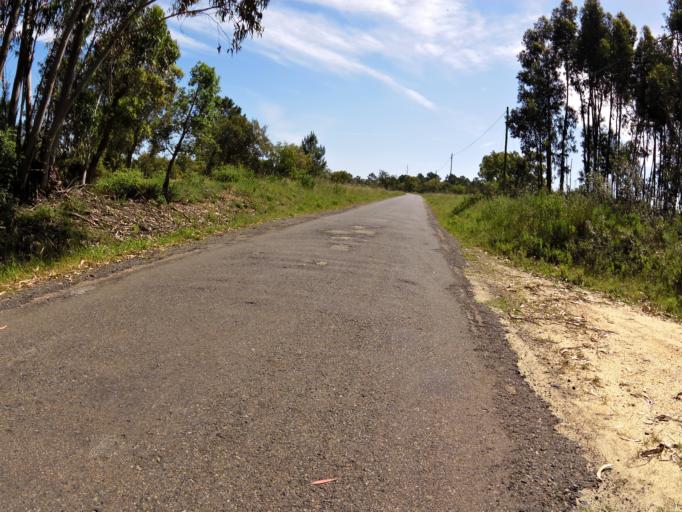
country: PT
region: Setubal
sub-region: Sines
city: Porto Covo
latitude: 37.9385
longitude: -8.7502
